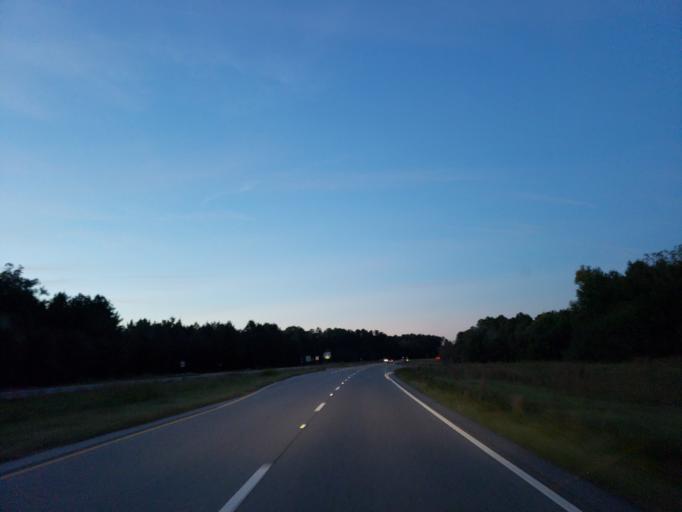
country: US
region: Mississippi
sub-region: Clarke County
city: Quitman
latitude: 31.8538
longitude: -88.7193
